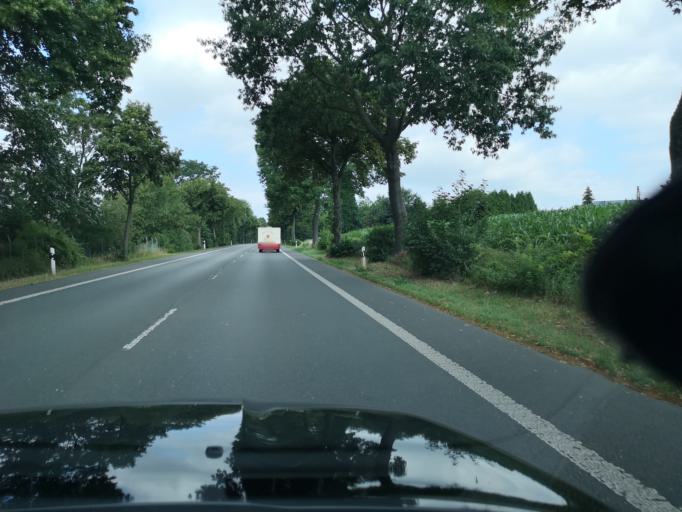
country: DE
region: North Rhine-Westphalia
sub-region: Regierungsbezirk Dusseldorf
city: Wesel
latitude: 51.6661
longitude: 6.6432
